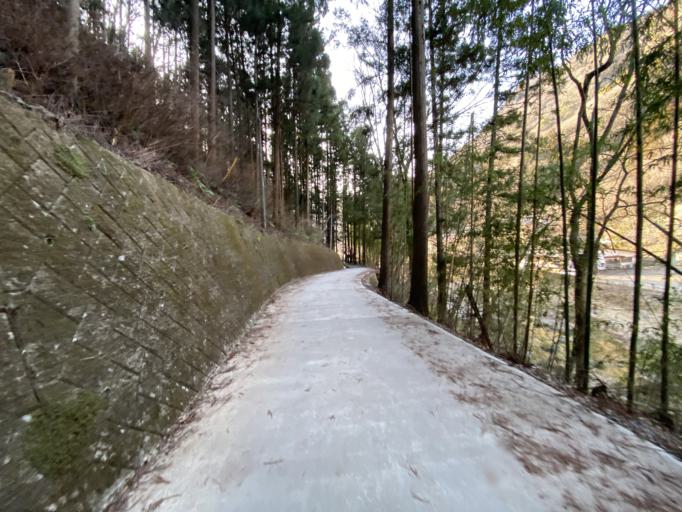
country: JP
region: Ibaraki
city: Daigo
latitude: 36.7645
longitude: 140.4037
